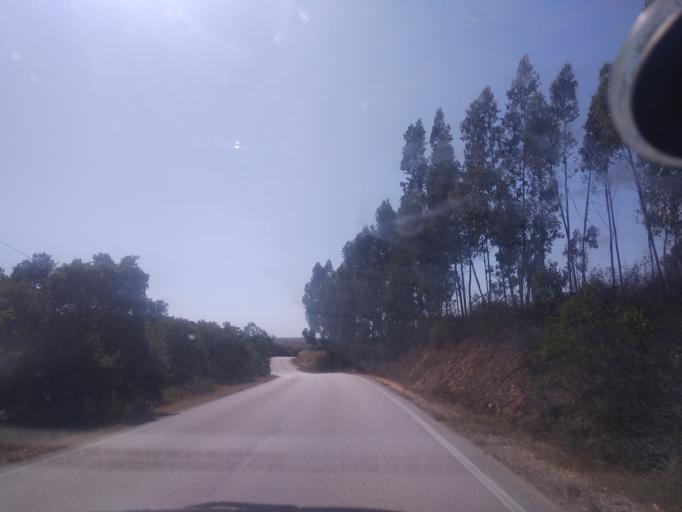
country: PT
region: Faro
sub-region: Aljezur
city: Aljezur
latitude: 37.2228
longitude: -8.8058
